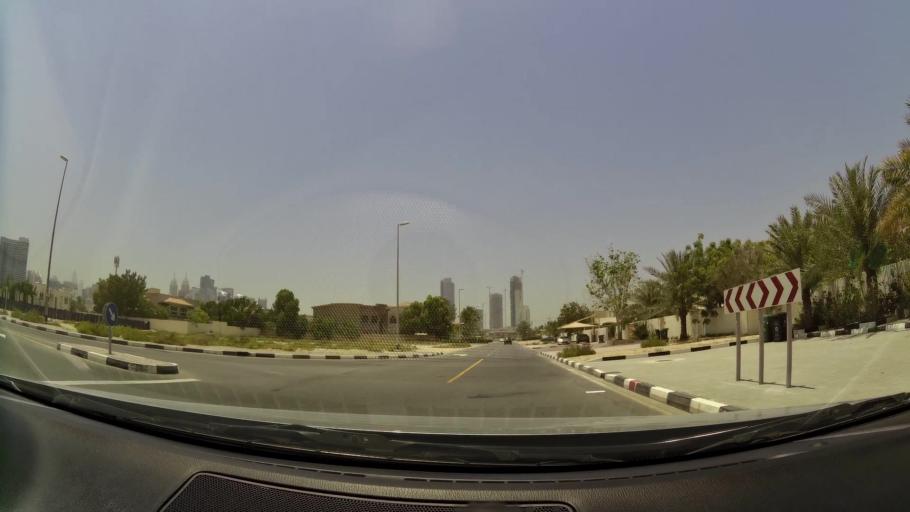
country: AE
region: Dubai
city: Dubai
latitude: 25.1014
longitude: 55.1902
